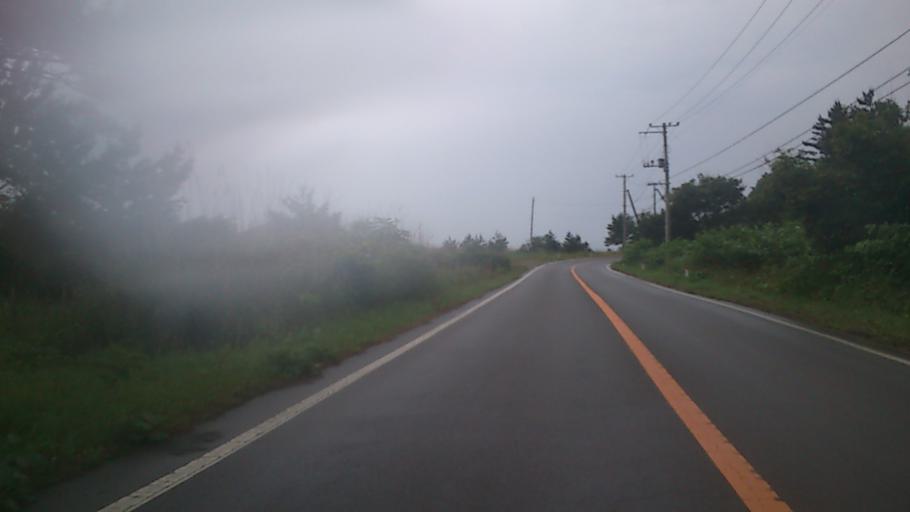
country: JP
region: Akita
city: Noshiromachi
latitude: 40.4507
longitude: 139.9428
